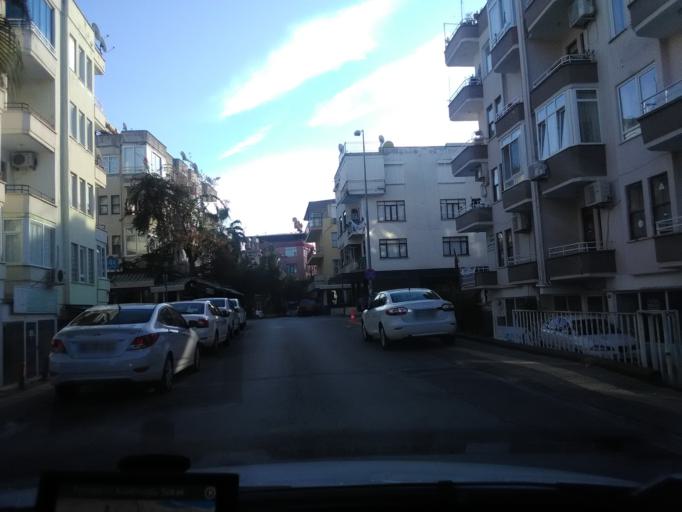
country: TR
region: Antalya
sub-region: Alanya
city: Alanya
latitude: 36.5451
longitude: 31.9907
